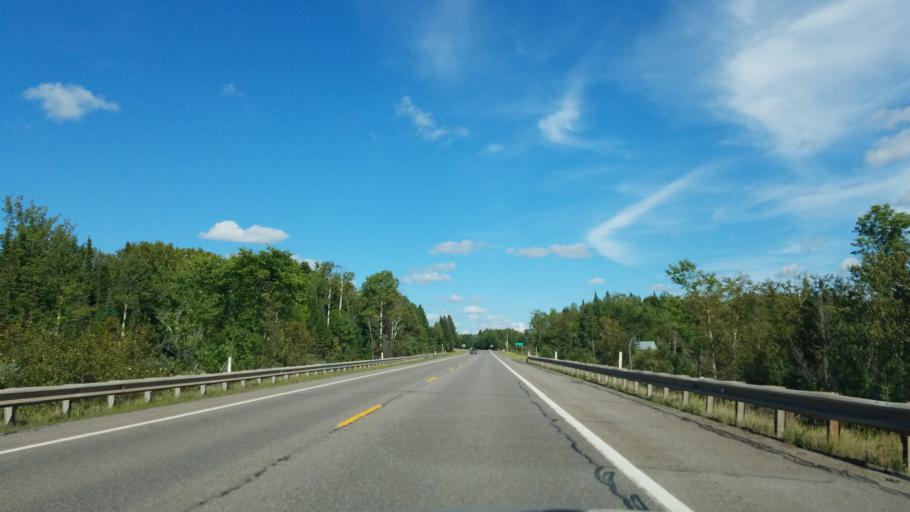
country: US
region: Michigan
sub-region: Baraga County
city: L'Anse
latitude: 46.5488
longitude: -88.5289
